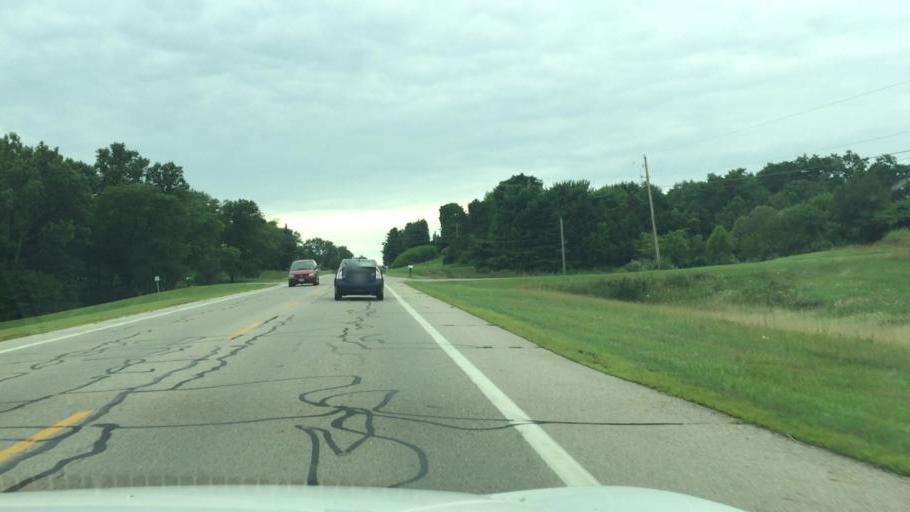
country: US
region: Ohio
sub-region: Champaign County
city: Mechanicsburg
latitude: 40.0784
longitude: -83.5922
